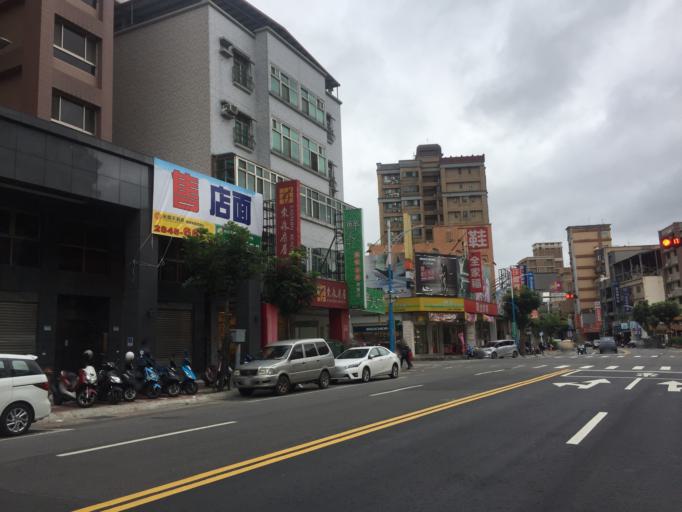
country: TW
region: Taipei
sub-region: Taipei
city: Banqiao
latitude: 25.0908
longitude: 121.4598
